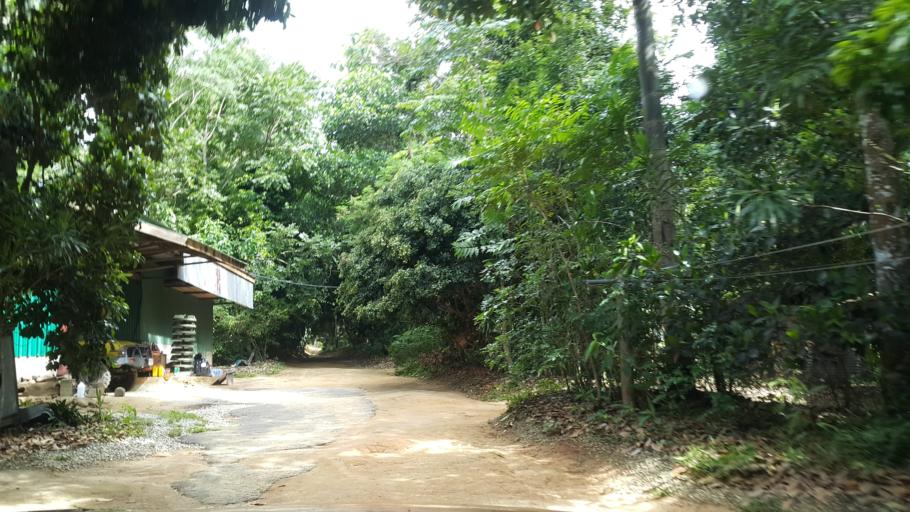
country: TH
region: Loei
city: Na Haeo
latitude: 17.5568
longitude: 100.9545
